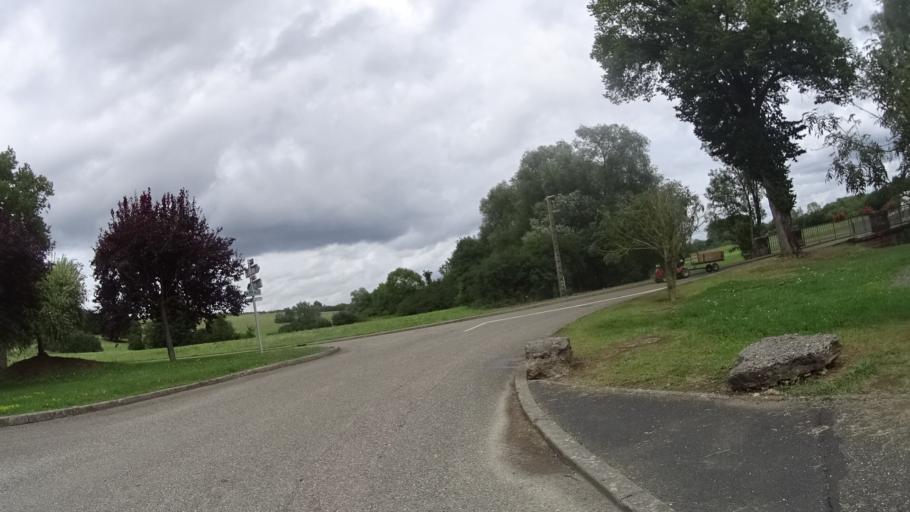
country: FR
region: Lorraine
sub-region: Departement de la Moselle
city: Lorquin
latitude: 48.6995
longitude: 6.9930
